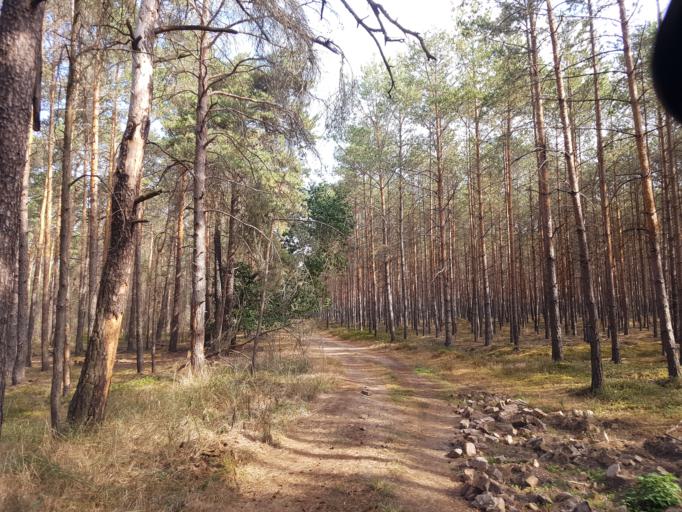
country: DE
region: Brandenburg
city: Finsterwalde
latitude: 51.5963
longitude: 13.7588
